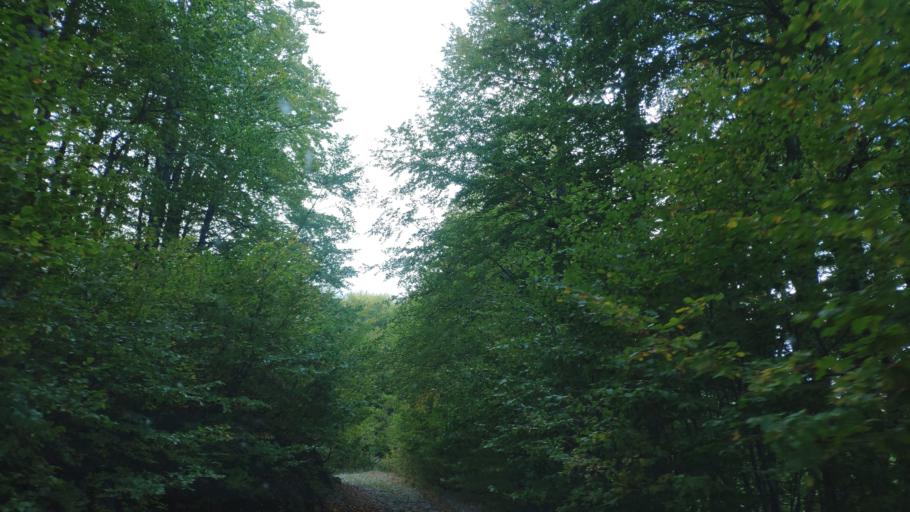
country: GR
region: West Macedonia
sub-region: Nomos Kastorias
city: Nestorio
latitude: 40.3084
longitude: 20.9164
